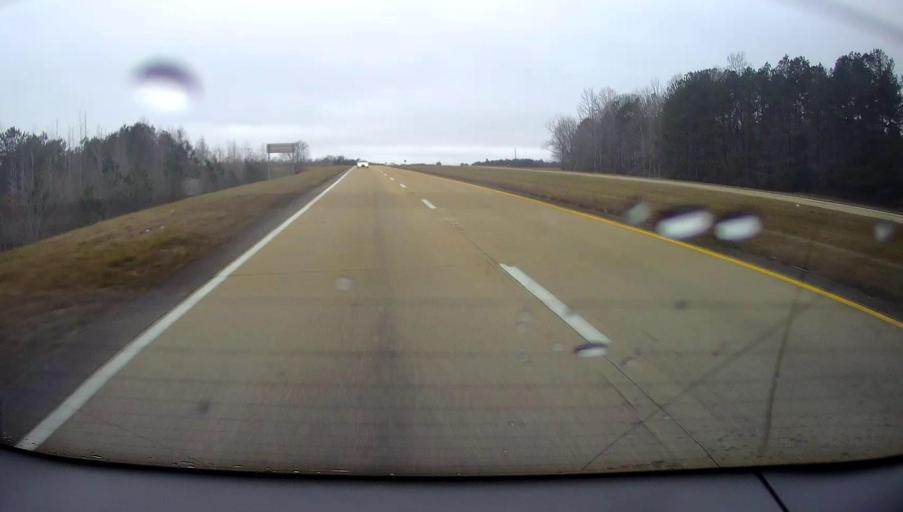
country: US
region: Mississippi
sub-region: Tishomingo County
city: Iuka
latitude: 34.7812
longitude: -88.1646
